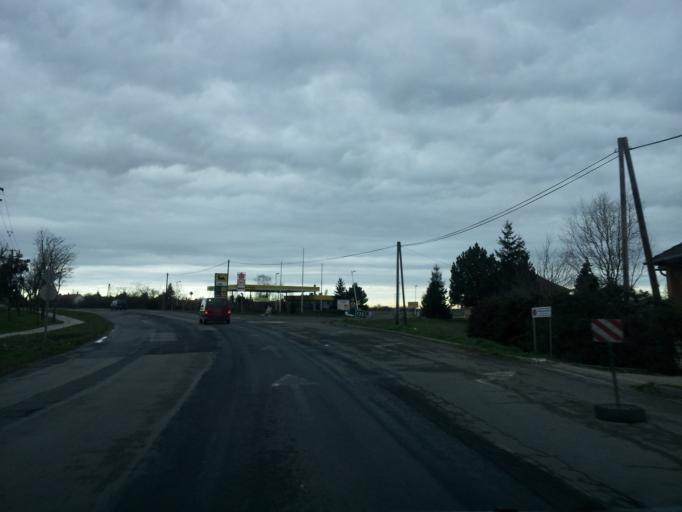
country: HU
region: Gyor-Moson-Sopron
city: Beled
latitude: 47.4758
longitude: 17.1652
